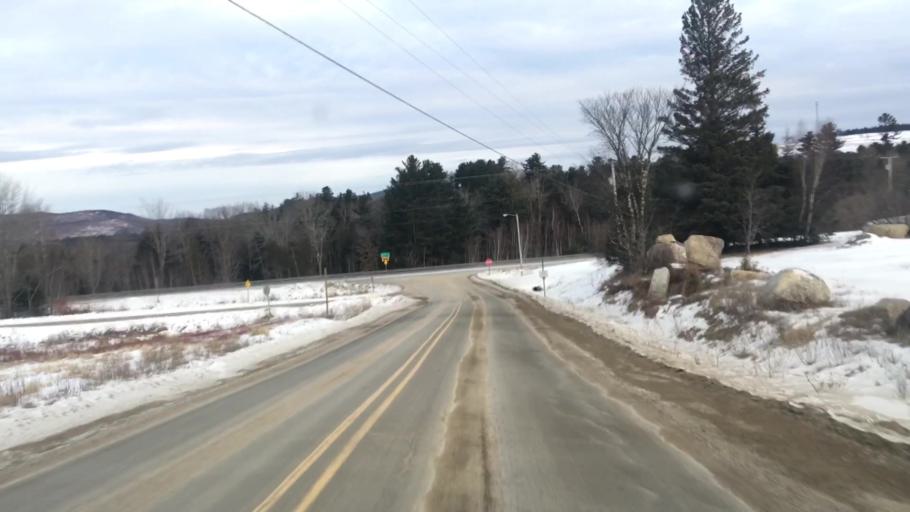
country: US
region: Maine
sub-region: Hancock County
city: Franklin
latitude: 44.8491
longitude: -68.3301
